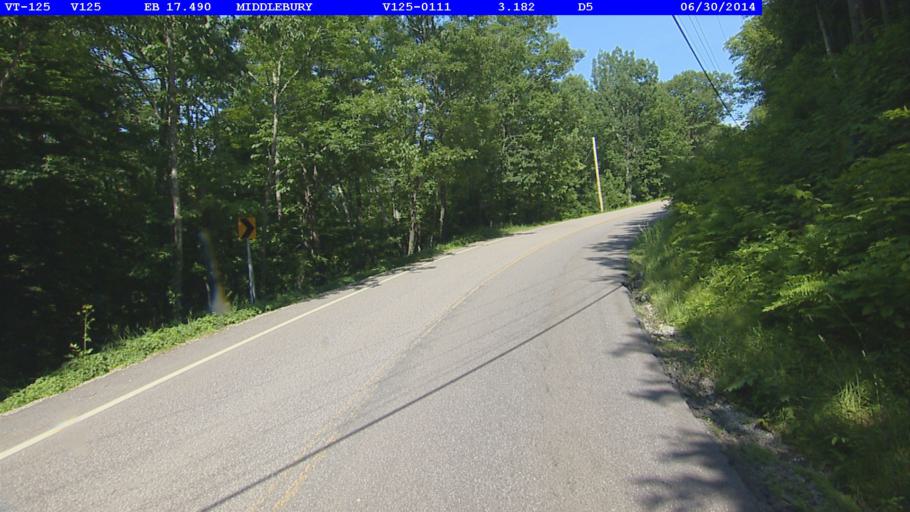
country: US
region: Vermont
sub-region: Addison County
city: Middlebury (village)
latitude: 43.9710
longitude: -73.0795
